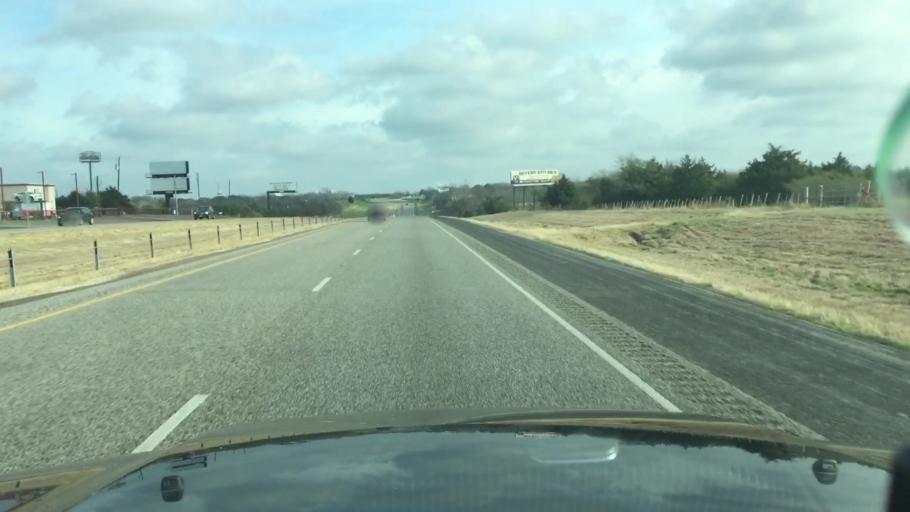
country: US
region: Texas
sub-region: Washington County
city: Brenham
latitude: 30.1394
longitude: -96.2778
